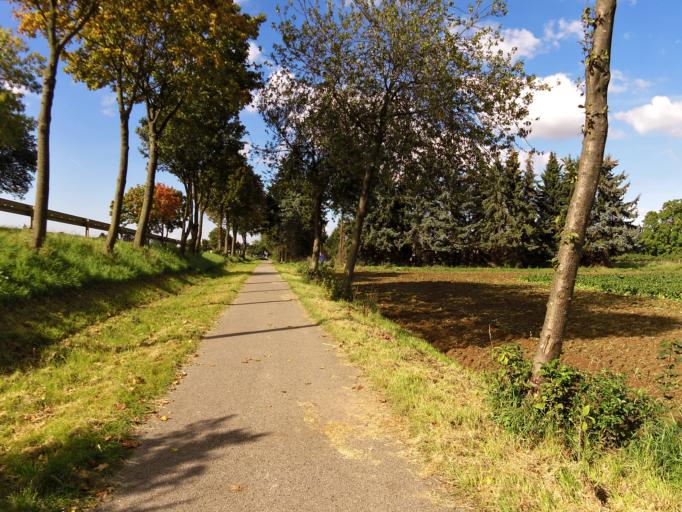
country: DE
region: North Rhine-Westphalia
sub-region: Regierungsbezirk Koln
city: Euskirchen
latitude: 50.6443
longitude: 6.8281
